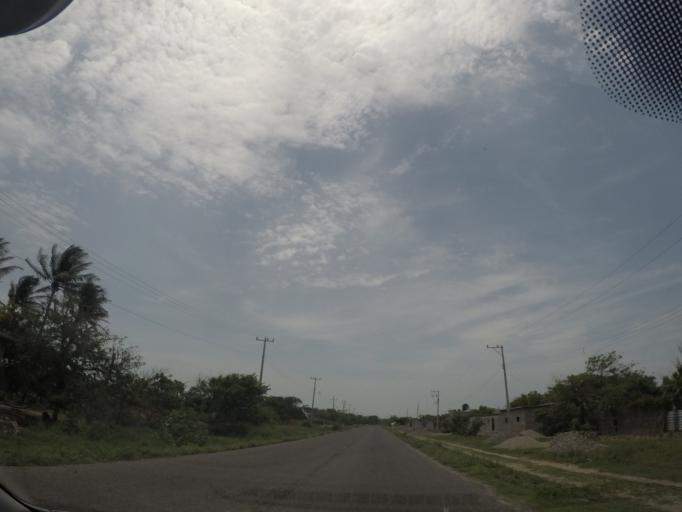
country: MX
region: Oaxaca
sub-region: San Mateo del Mar
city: Colonia Juarez
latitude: 16.2095
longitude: -95.0195
